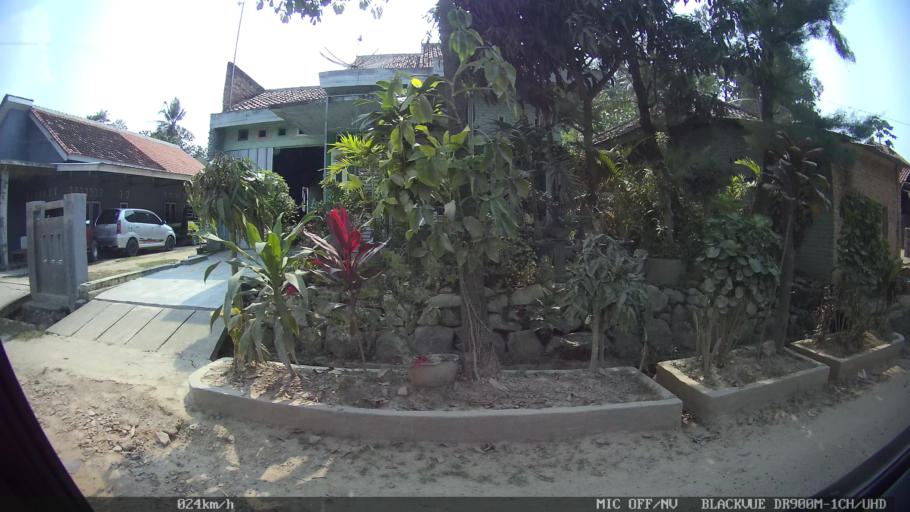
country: ID
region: Lampung
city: Pringsewu
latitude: -5.4016
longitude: 104.9929
